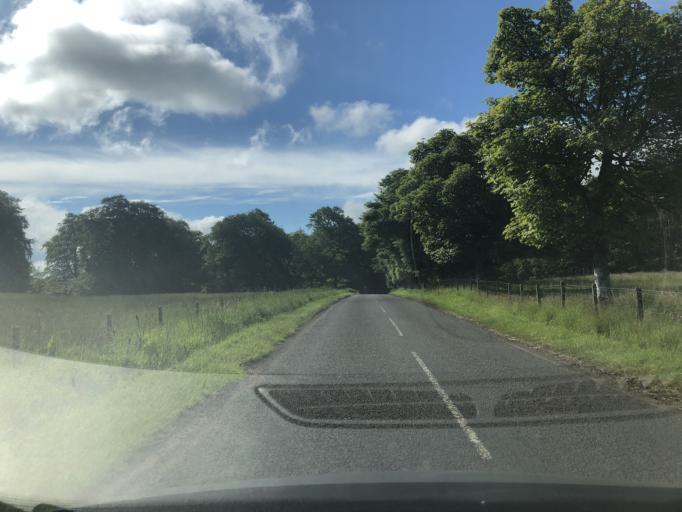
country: GB
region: Scotland
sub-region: Angus
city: Kirriemuir
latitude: 56.7406
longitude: -3.0089
